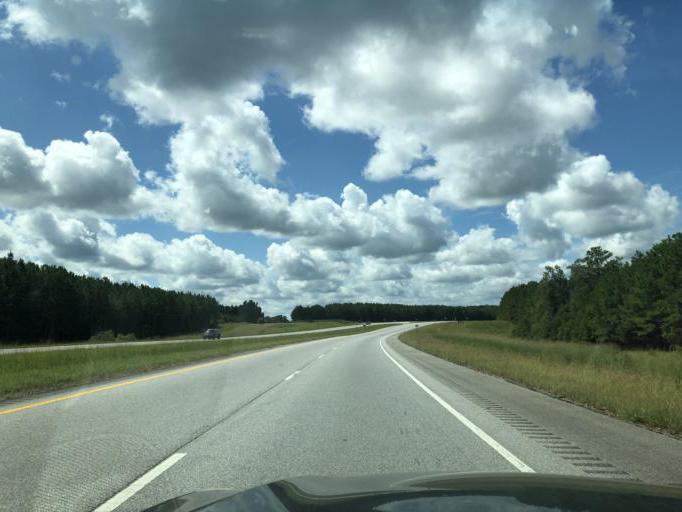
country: US
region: Alabama
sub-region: Russell County
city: Ladonia
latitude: 32.2154
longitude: -85.1685
